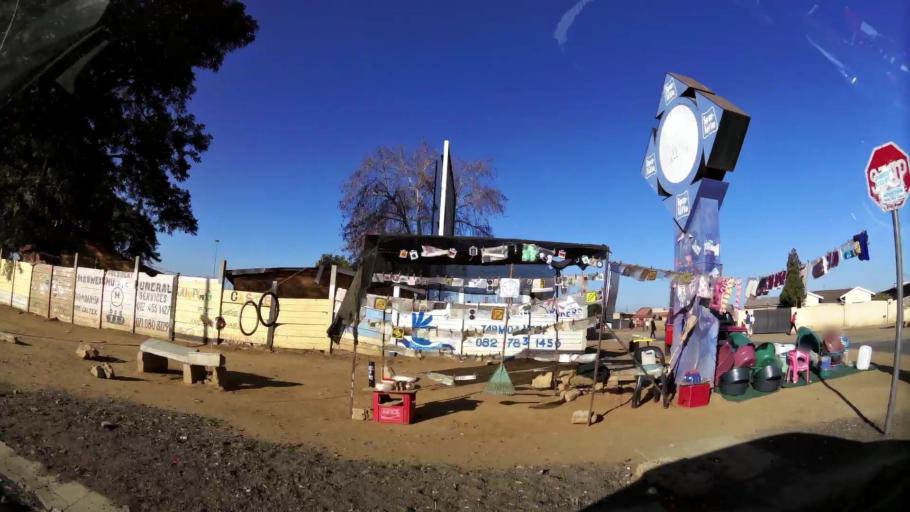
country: ZA
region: Gauteng
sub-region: Ekurhuleni Metropolitan Municipality
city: Tembisa
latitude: -26.0093
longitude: 28.2419
